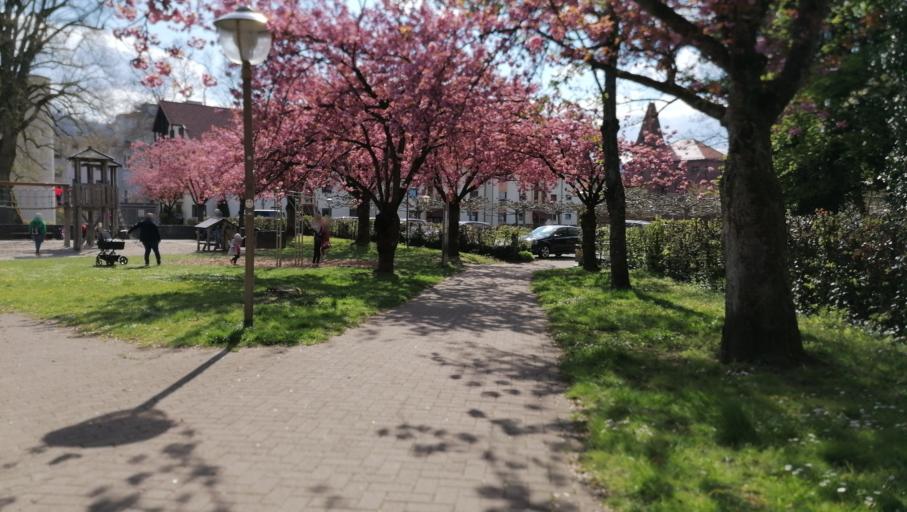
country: DE
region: Baden-Wuerttemberg
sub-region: Freiburg Region
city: Bad Sackingen
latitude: 47.5512
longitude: 7.9480
